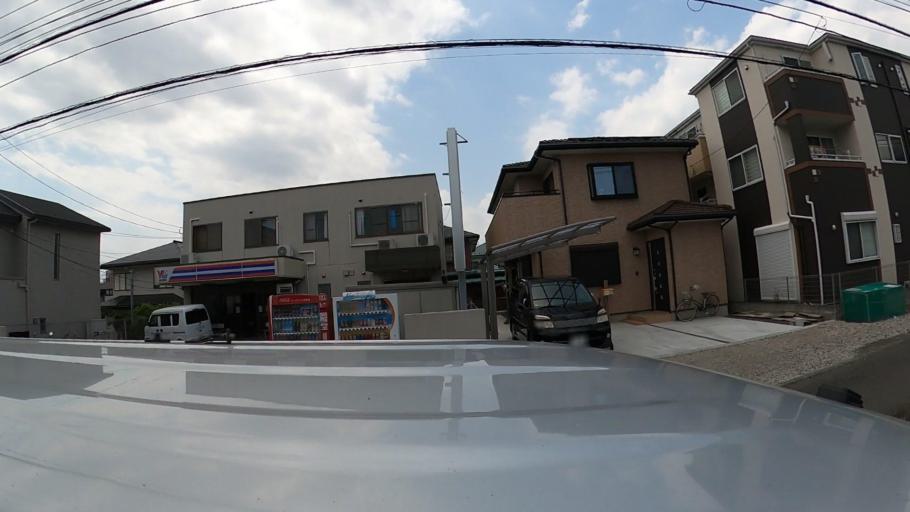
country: JP
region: Kanagawa
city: Chigasaki
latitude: 35.3707
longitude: 139.3901
